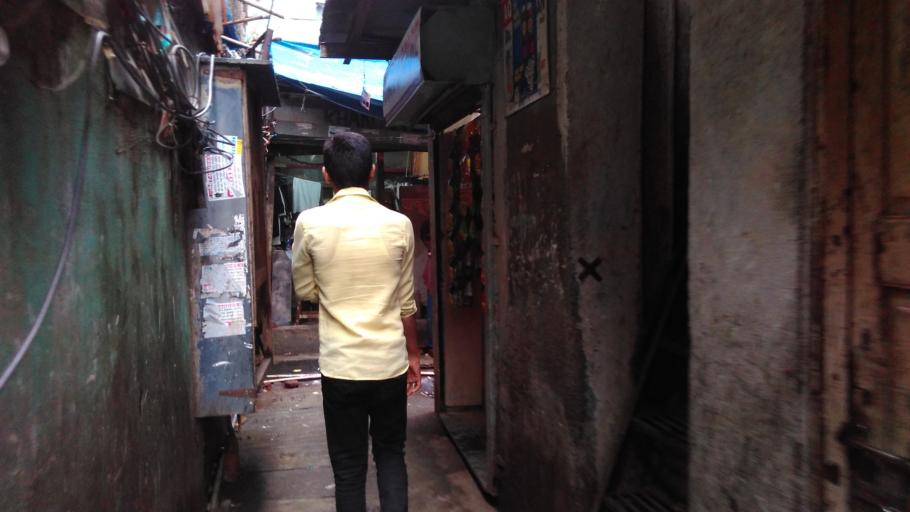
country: IN
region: Maharashtra
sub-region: Mumbai Suburban
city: Mumbai
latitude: 19.0627
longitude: 72.8791
